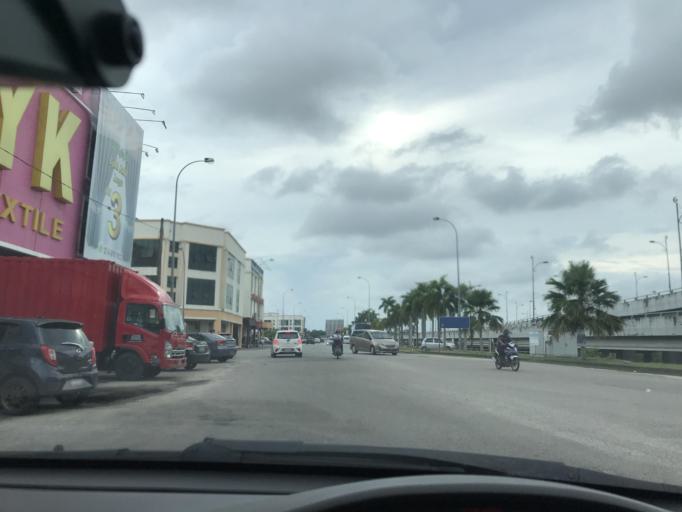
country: MY
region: Kelantan
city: Kota Bharu
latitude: 6.1150
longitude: 102.2338
